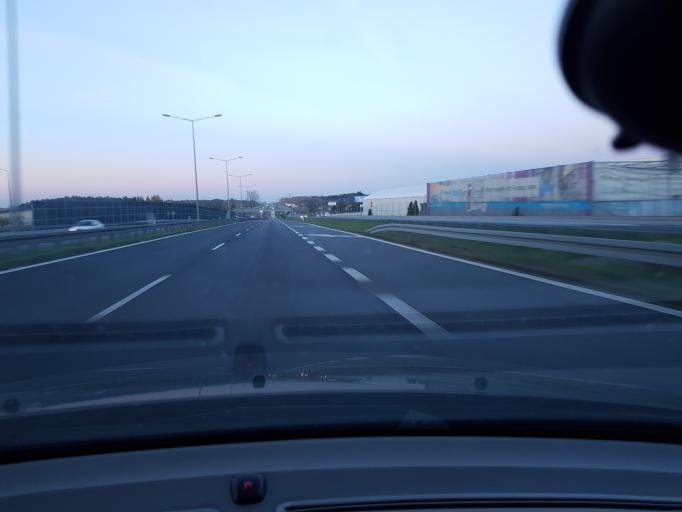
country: PL
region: Masovian Voivodeship
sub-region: Powiat zyrardowski
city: Mszczonow
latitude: 51.9376
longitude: 20.4787
